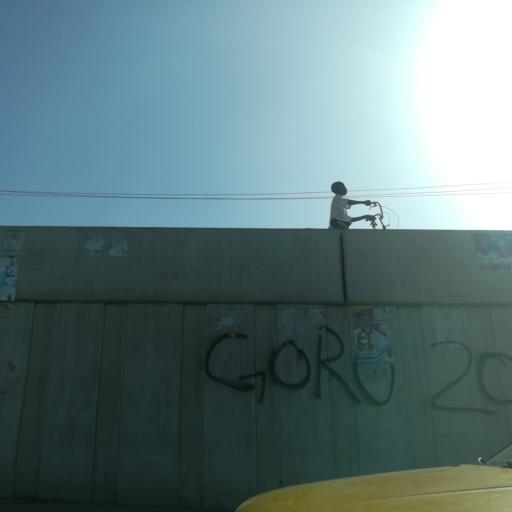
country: NG
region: Kano
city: Kano
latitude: 12.0306
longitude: 8.5002
